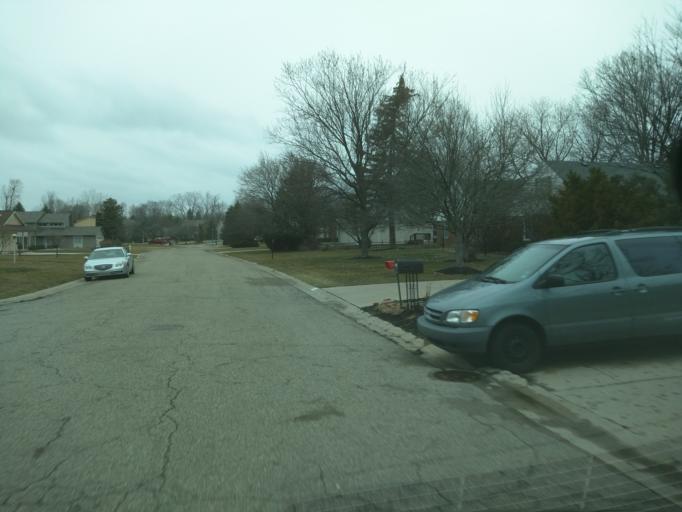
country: US
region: Michigan
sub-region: Eaton County
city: Waverly
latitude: 42.7600
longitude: -84.6277
